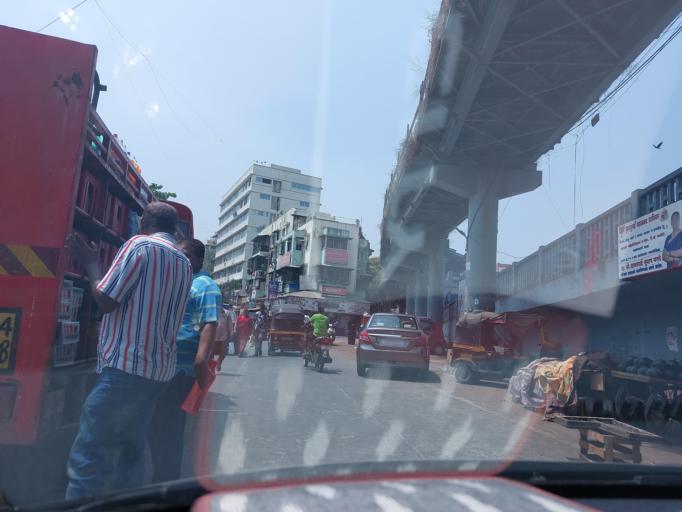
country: IN
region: Maharashtra
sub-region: Mumbai Suburban
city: Mumbai
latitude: 19.0625
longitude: 72.8983
